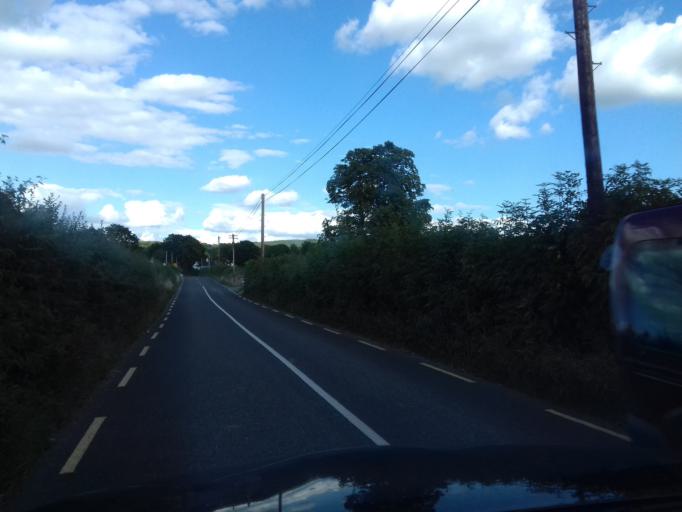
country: IE
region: Leinster
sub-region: Kilkenny
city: Thomastown
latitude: 52.5336
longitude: -7.1108
